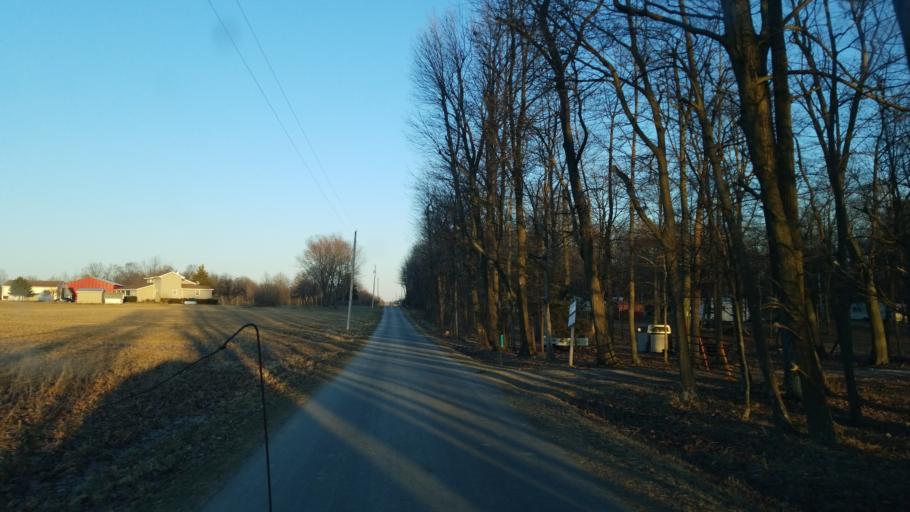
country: US
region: Ohio
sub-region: Hardin County
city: Kenton
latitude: 40.6287
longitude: -83.4665
